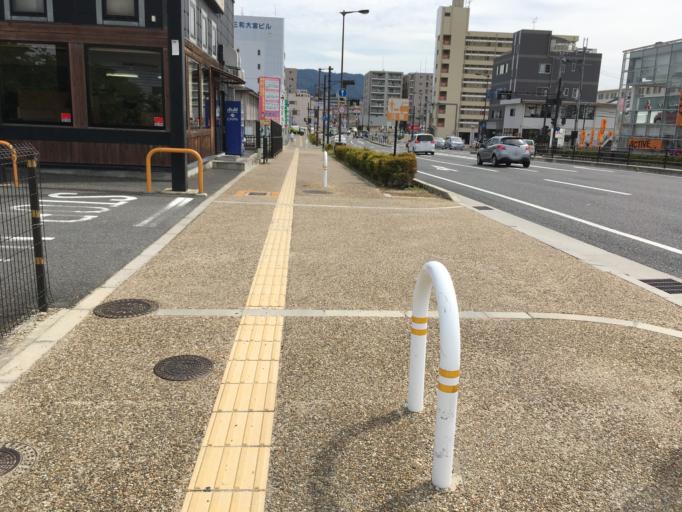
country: JP
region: Nara
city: Nara-shi
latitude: 34.6820
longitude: 135.8073
